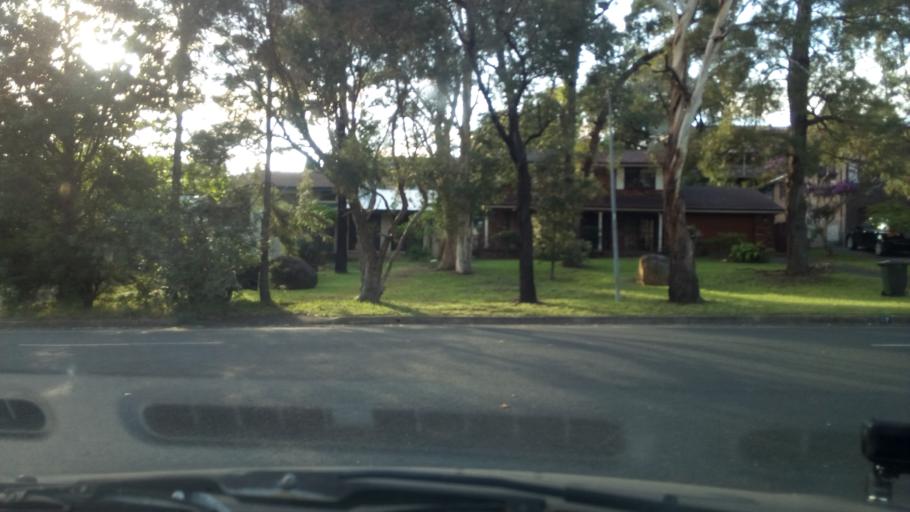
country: AU
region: New South Wales
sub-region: Wollongong
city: Mount Ousley
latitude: -34.3908
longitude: 150.8743
